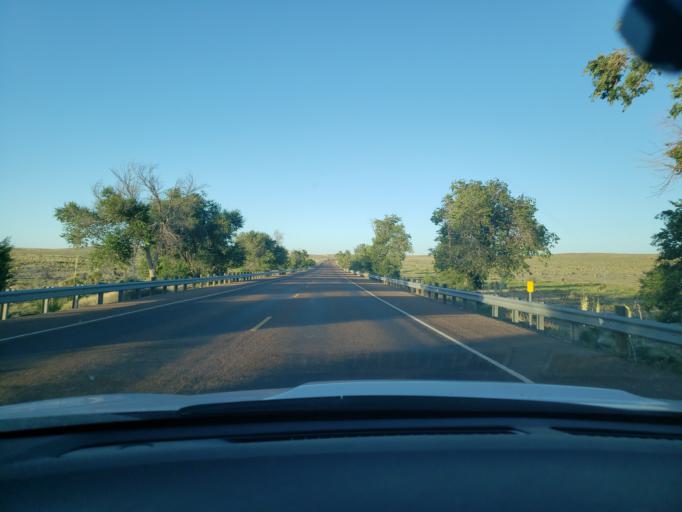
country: US
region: Texas
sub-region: El Paso County
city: Homestead Meadows South
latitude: 31.8310
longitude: -105.8654
